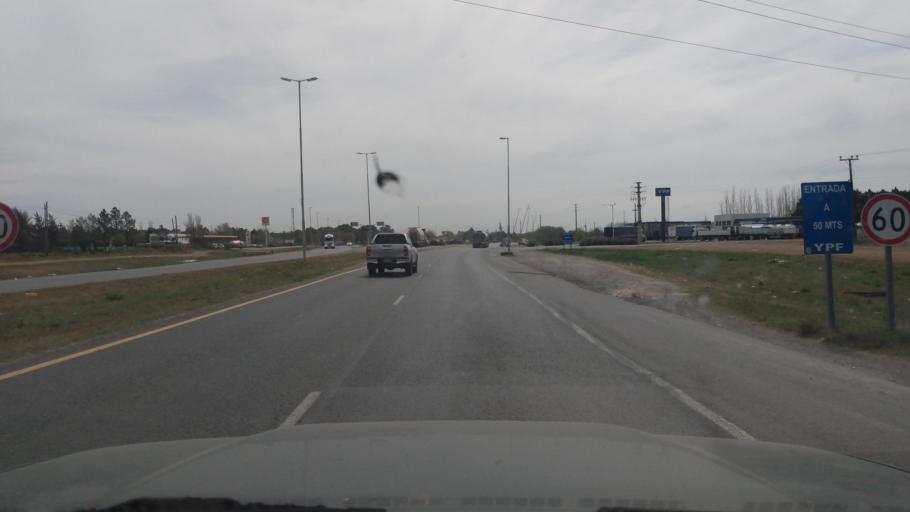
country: AR
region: Buenos Aires
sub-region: Partido de Lujan
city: Lujan
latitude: -34.5596
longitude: -59.0366
